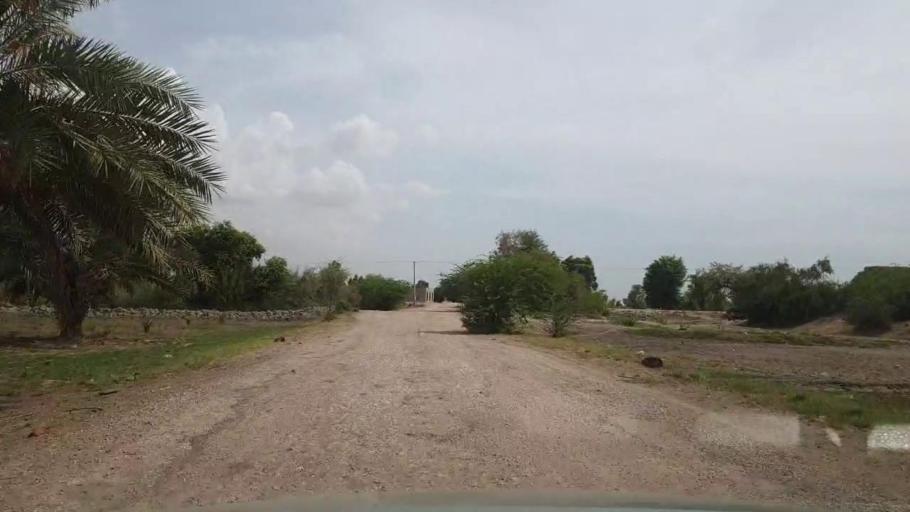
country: PK
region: Sindh
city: Kot Diji
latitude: 27.1116
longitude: 69.0223
